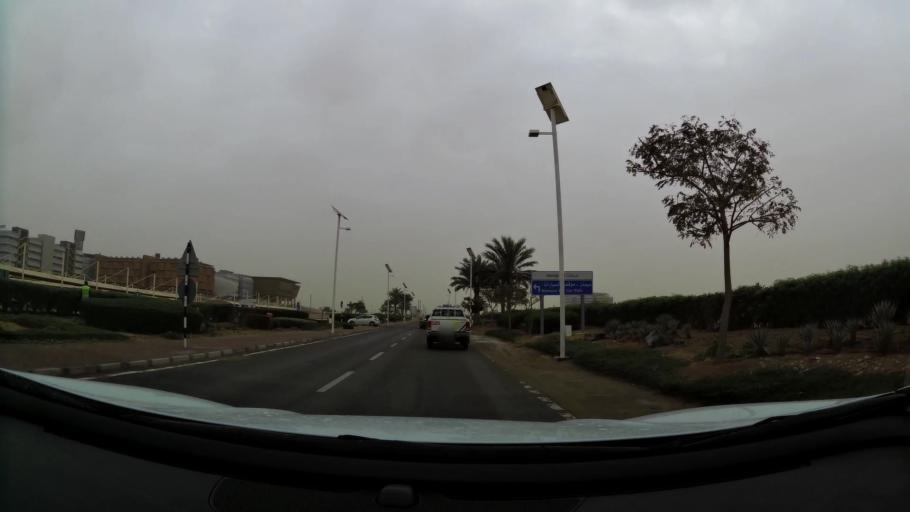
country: AE
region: Abu Dhabi
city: Abu Dhabi
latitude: 24.4330
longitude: 54.6143
